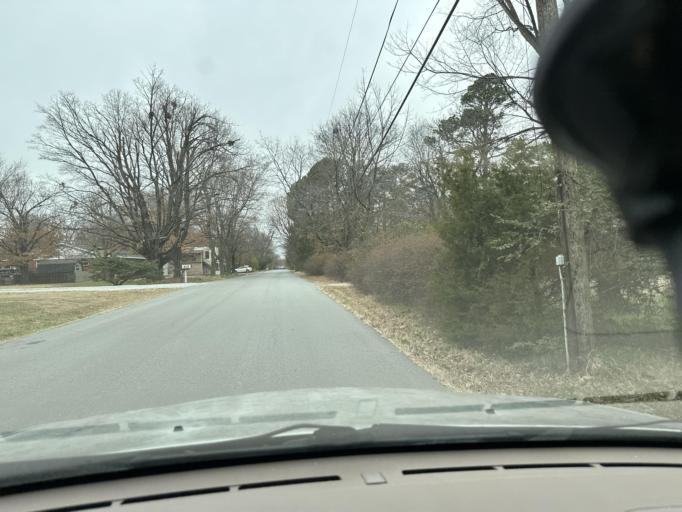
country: US
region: Arkansas
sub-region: Washington County
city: Fayetteville
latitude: 36.0904
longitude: -94.1571
